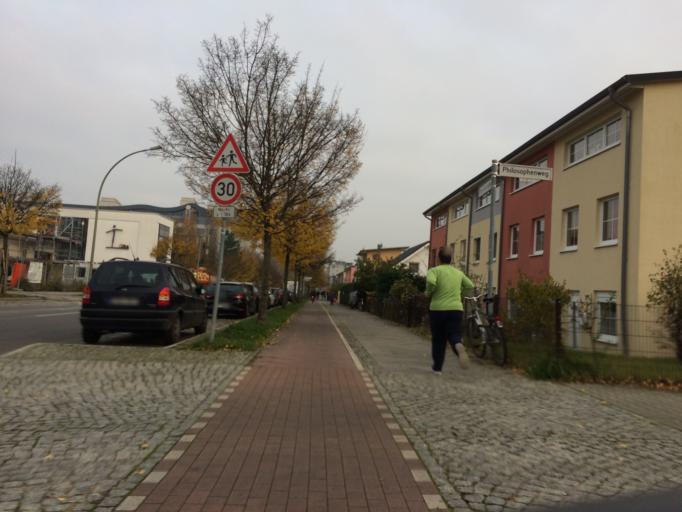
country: DE
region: Berlin
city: Lichtenberg
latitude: 52.5206
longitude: 13.4878
